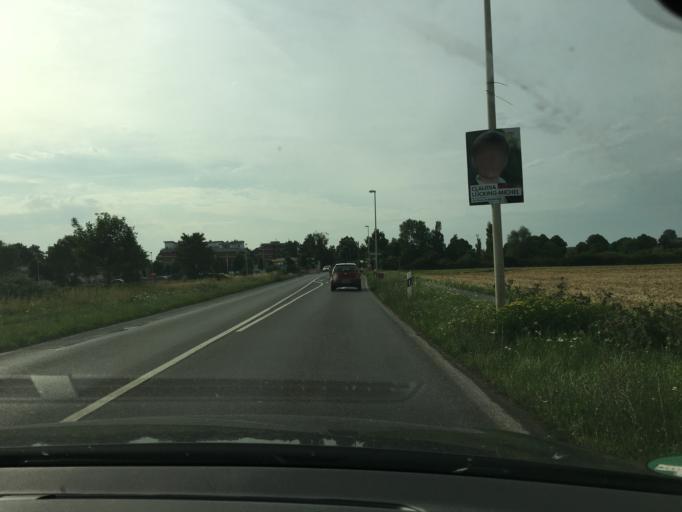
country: DE
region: North Rhine-Westphalia
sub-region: Regierungsbezirk Koln
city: Bonn
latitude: 50.7608
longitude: 7.0600
